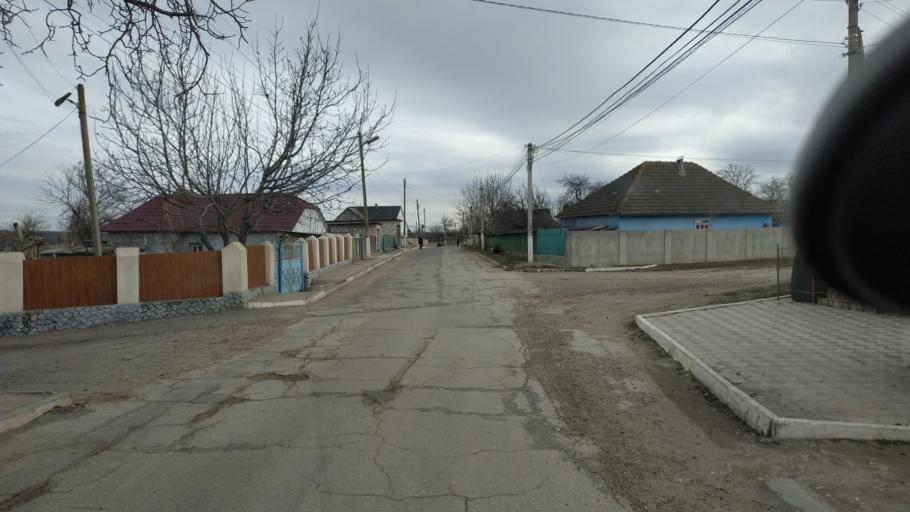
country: MD
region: Telenesti
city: Cocieri
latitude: 47.3826
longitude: 29.1170
